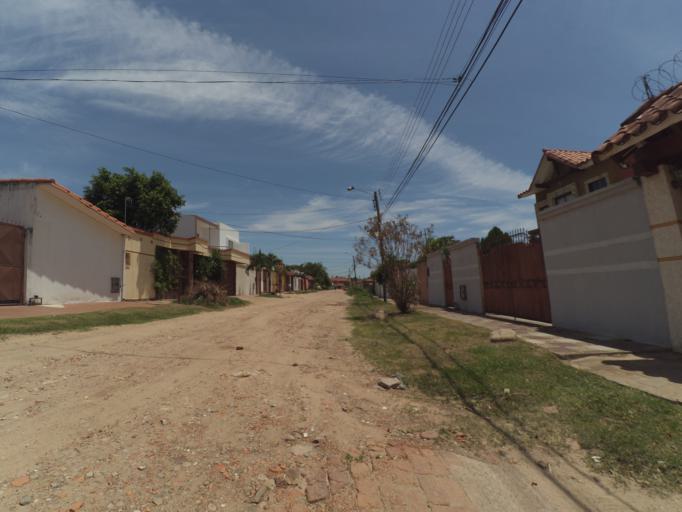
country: BO
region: Santa Cruz
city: Santa Cruz de la Sierra
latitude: -17.8128
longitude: -63.2229
